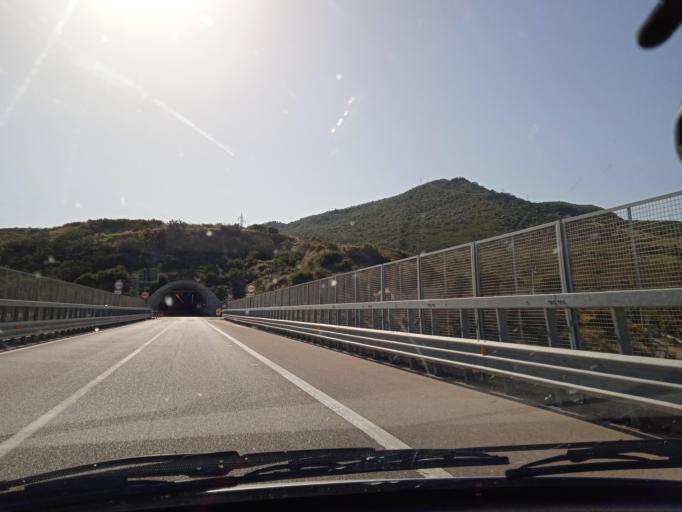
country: IT
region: Sicily
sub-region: Palermo
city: Finale
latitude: 38.0078
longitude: 14.1814
